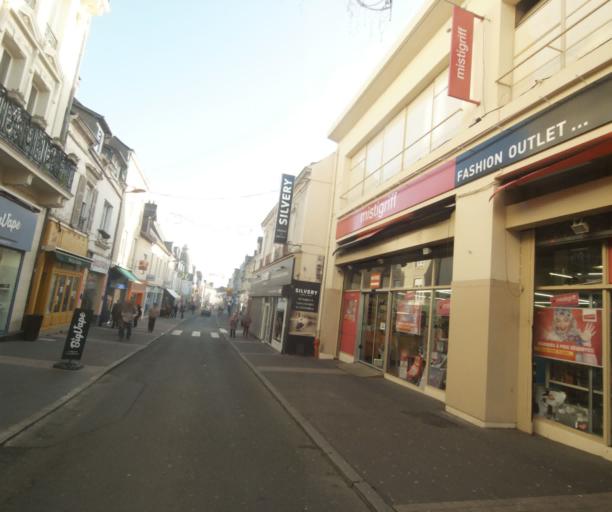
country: FR
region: Pays de la Loire
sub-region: Departement de la Sarthe
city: Le Mans
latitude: 48.0007
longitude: 0.1983
